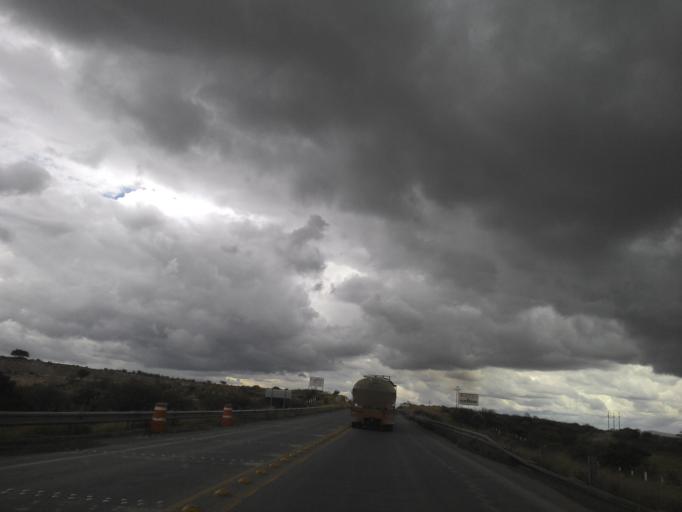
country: MX
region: Zacatecas
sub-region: Rio Grande
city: Los Condes
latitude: 23.8702
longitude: -103.0840
